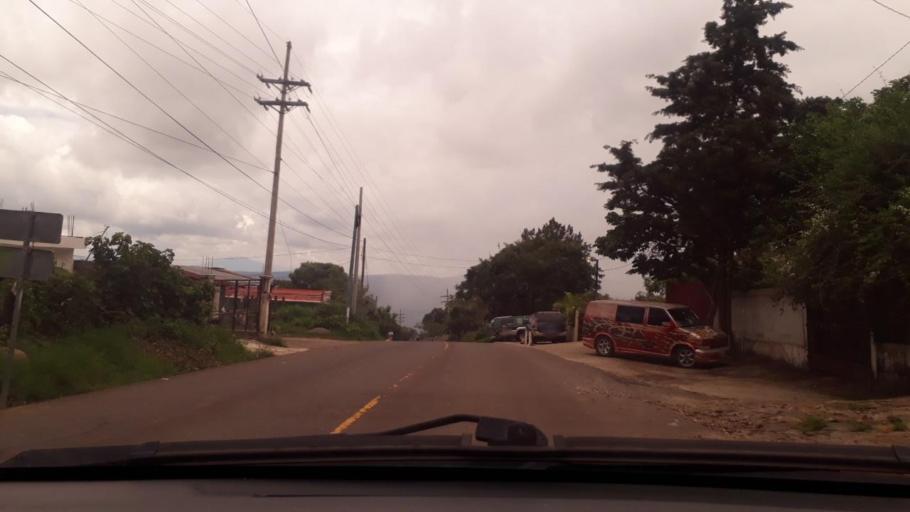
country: GT
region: Jutiapa
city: Conguaco
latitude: 14.0565
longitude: -90.0491
